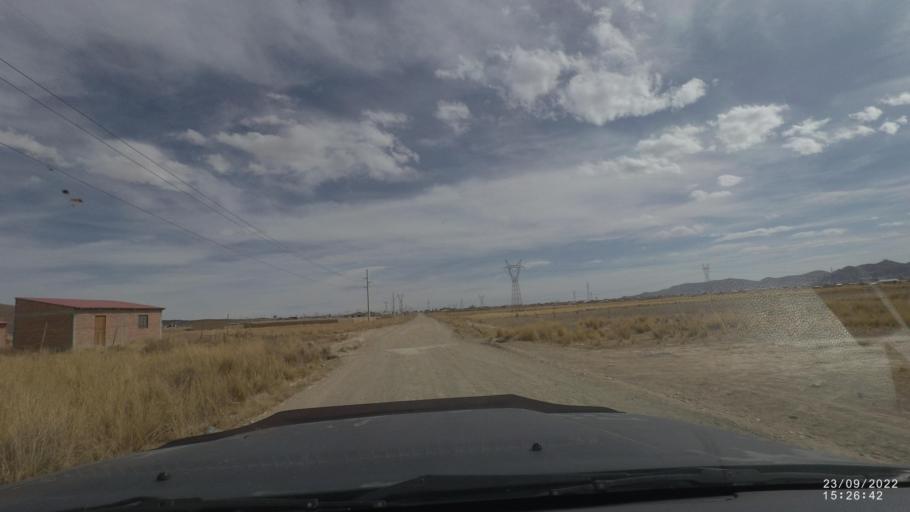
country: BO
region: Oruro
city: Oruro
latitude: -17.9560
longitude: -67.0406
